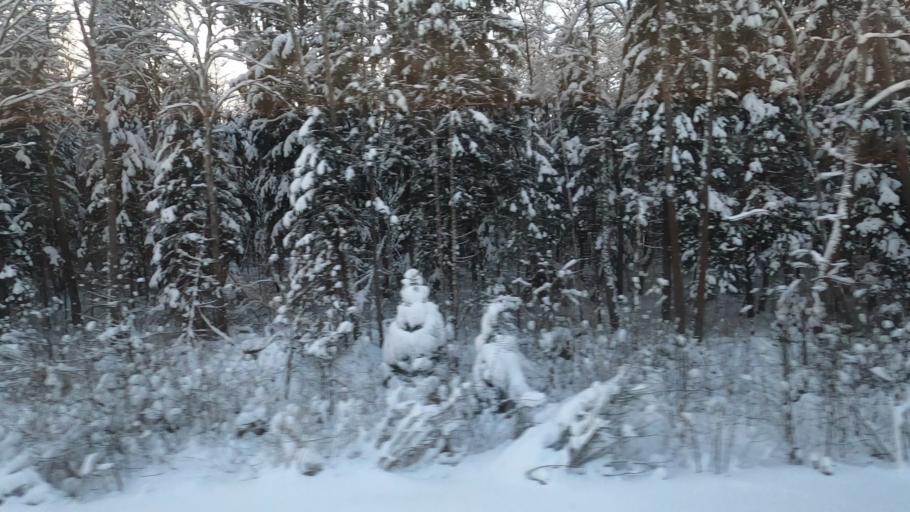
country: RU
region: Moskovskaya
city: Novo-Nikol'skoye
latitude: 56.5975
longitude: 37.5666
